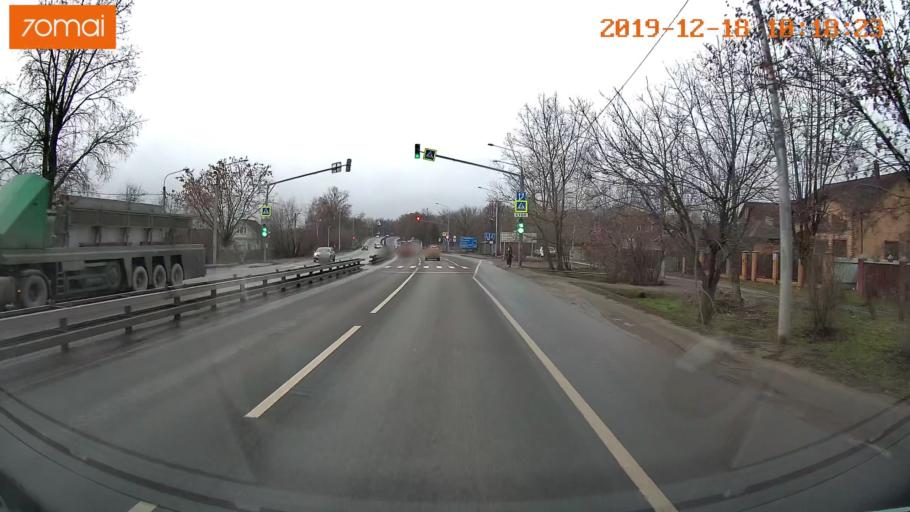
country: RU
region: Moskovskaya
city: Dubrovitsy
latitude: 55.3986
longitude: 37.4407
